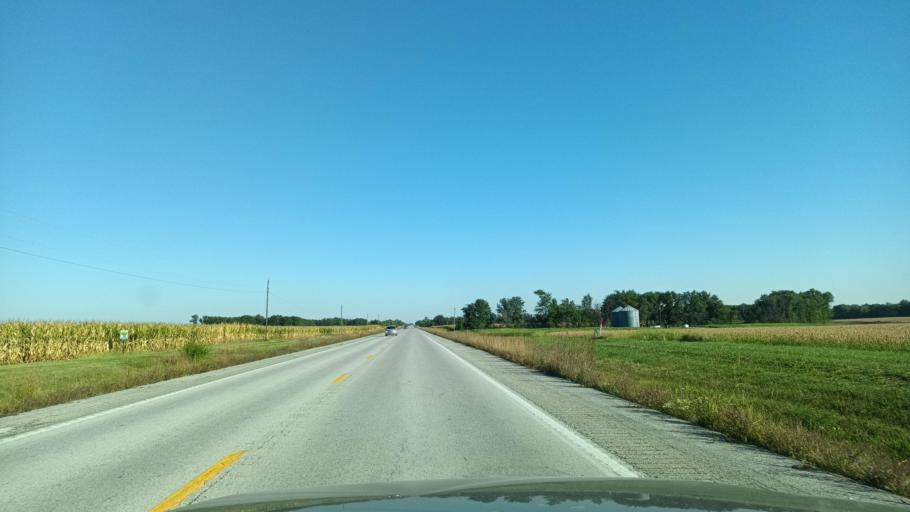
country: US
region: Missouri
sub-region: Audrain County
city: Vandalia
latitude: 39.3273
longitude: -91.6431
